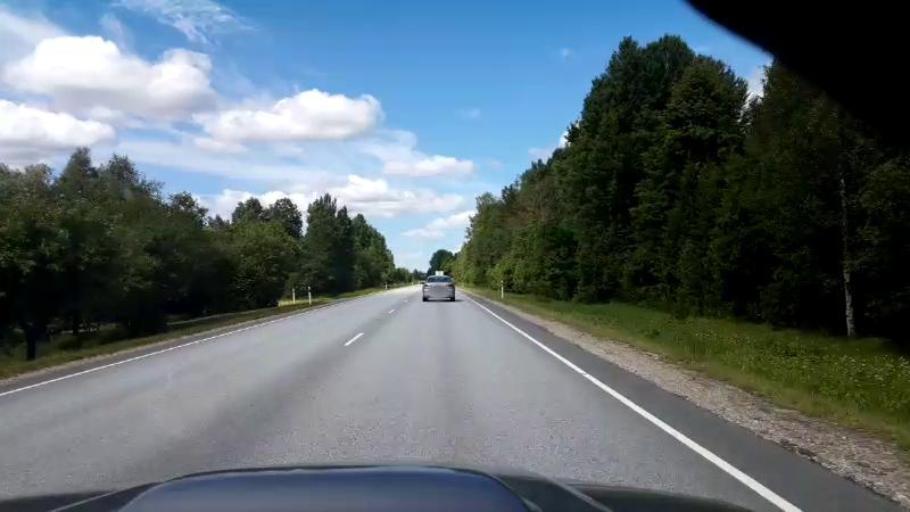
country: EE
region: Paernumaa
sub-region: Halinga vald
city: Parnu-Jaagupi
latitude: 58.5551
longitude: 24.5285
